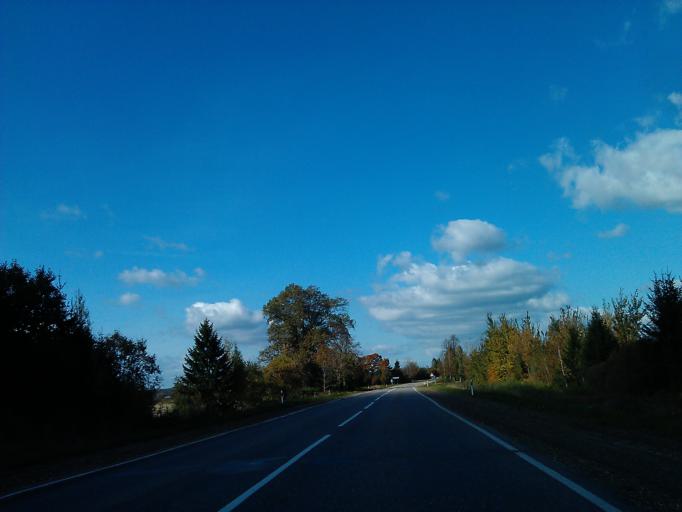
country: LV
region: Varkava
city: Vecvarkava
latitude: 56.1607
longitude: 26.3339
